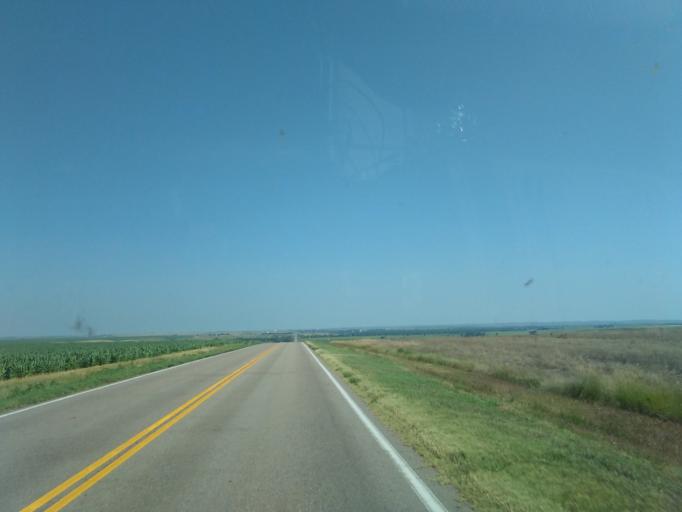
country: US
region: Nebraska
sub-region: Dundy County
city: Benkelman
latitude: 39.9767
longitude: -101.5418
